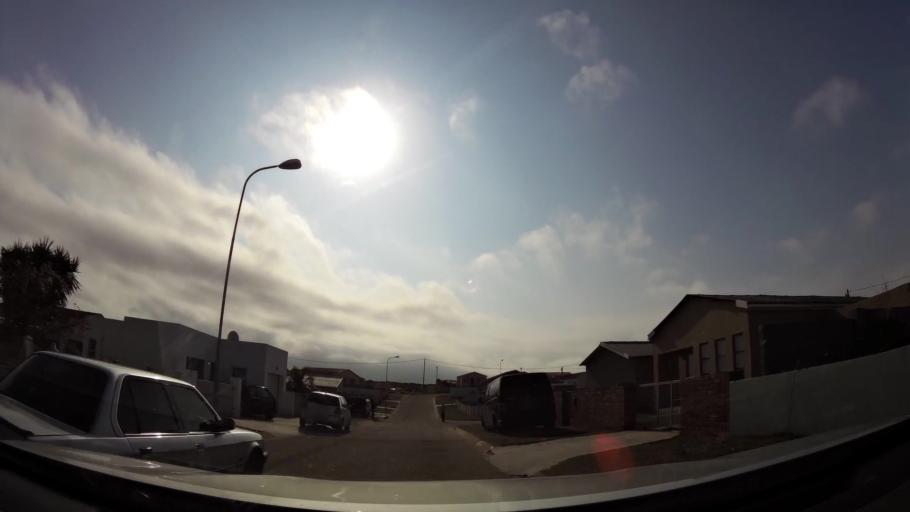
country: ZA
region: Eastern Cape
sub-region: Nelson Mandela Bay Metropolitan Municipality
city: Port Elizabeth
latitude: -33.9166
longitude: 25.5339
